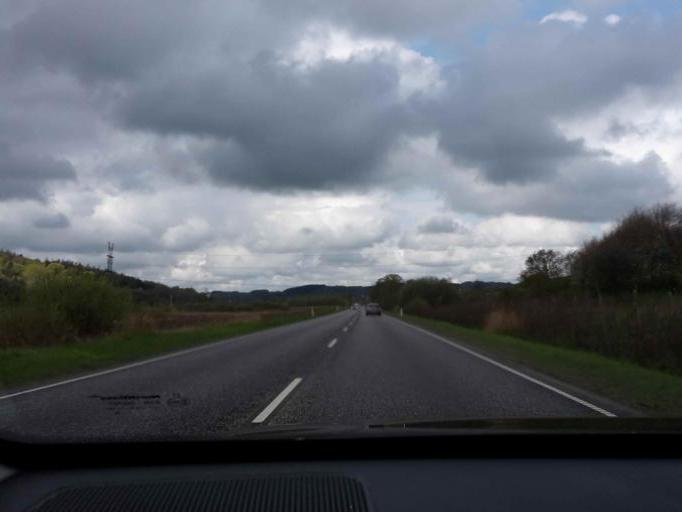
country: DK
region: South Denmark
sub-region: Vejle Kommune
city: Vejle
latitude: 55.7075
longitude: 9.4862
